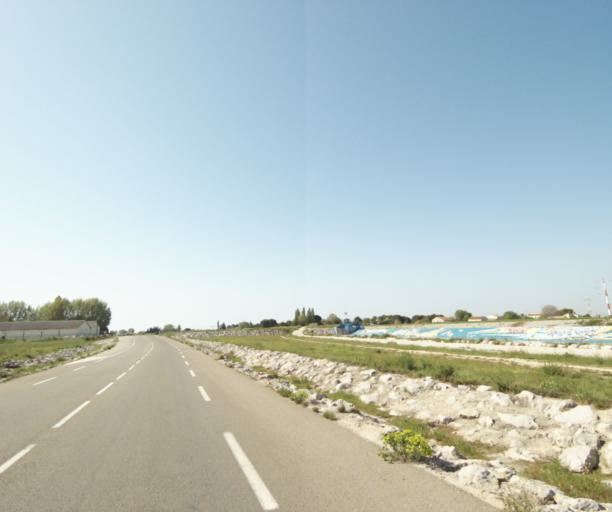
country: FR
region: Languedoc-Roussillon
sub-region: Departement de l'Herault
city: Lattes
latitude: 43.5876
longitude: 3.9082
